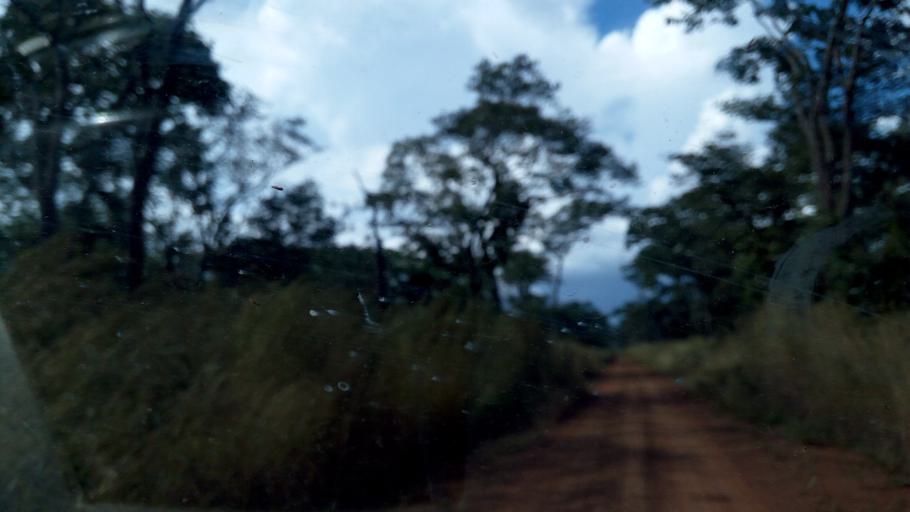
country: ZM
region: Northern
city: Kaputa
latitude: -8.1845
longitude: 29.0844
